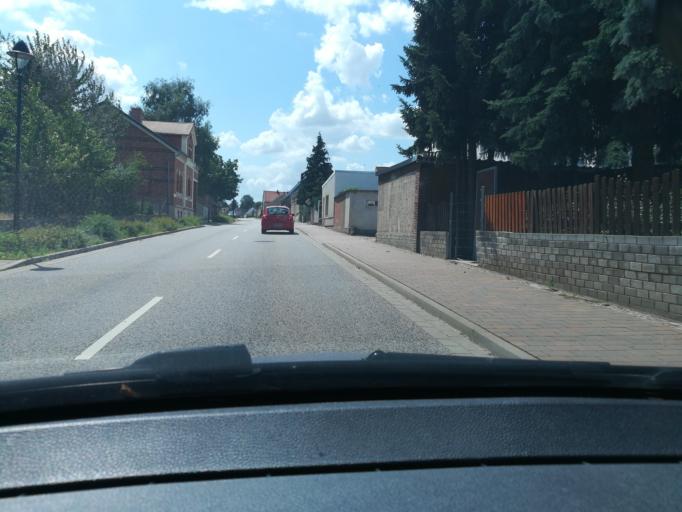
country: DE
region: Saxony-Anhalt
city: Zielitz
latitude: 52.2892
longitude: 11.6809
